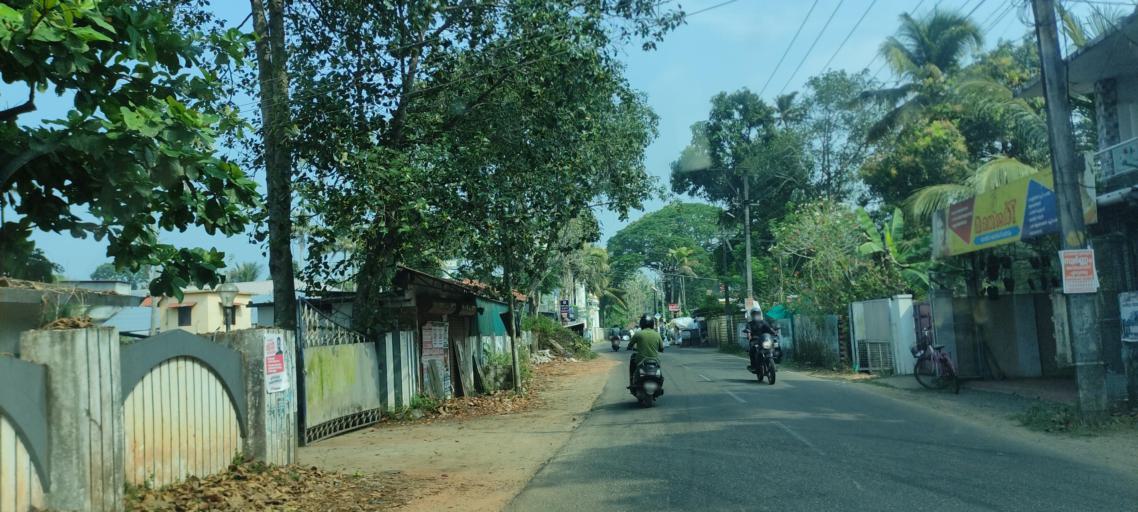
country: IN
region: Kerala
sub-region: Alappuzha
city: Kutiatodu
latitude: 9.7759
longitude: 76.3053
